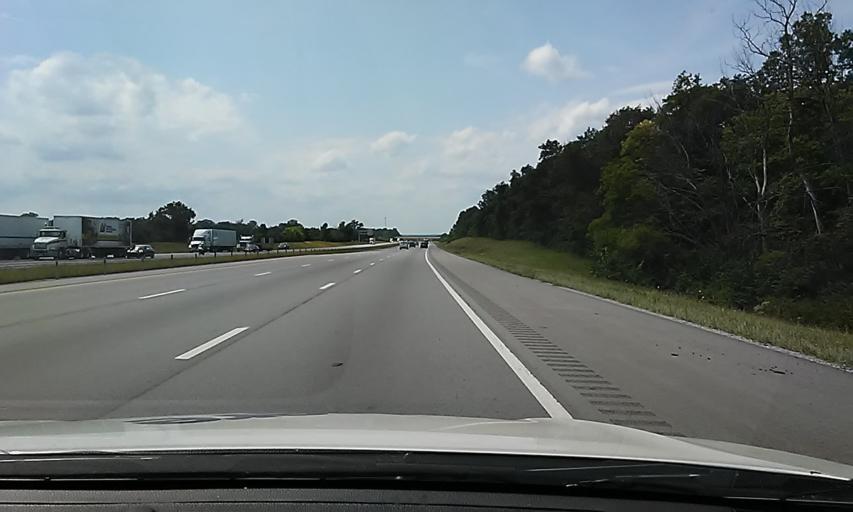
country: US
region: Ohio
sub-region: Clark County
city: Enon
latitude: 39.8925
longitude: -83.8895
